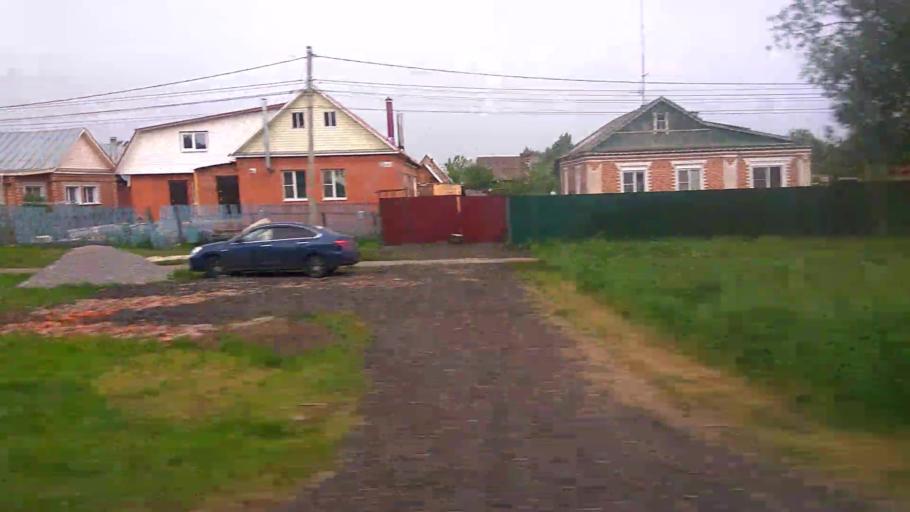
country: RU
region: Moskovskaya
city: Lukhovitsy
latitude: 54.9356
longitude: 39.0110
